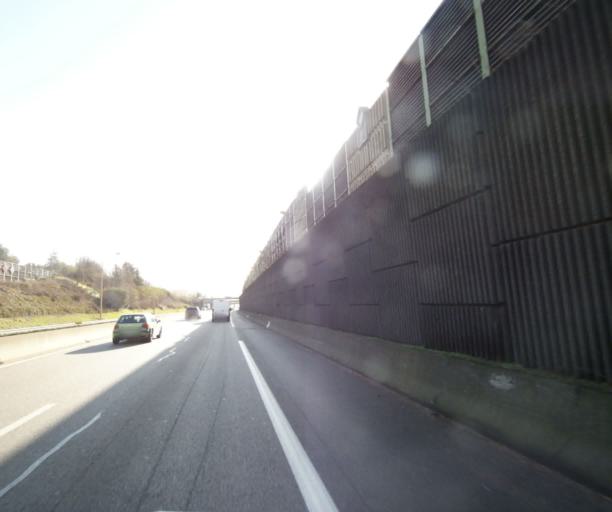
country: FR
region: Rhone-Alpes
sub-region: Departement de la Loire
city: Roanne
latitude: 46.0592
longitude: 4.0701
